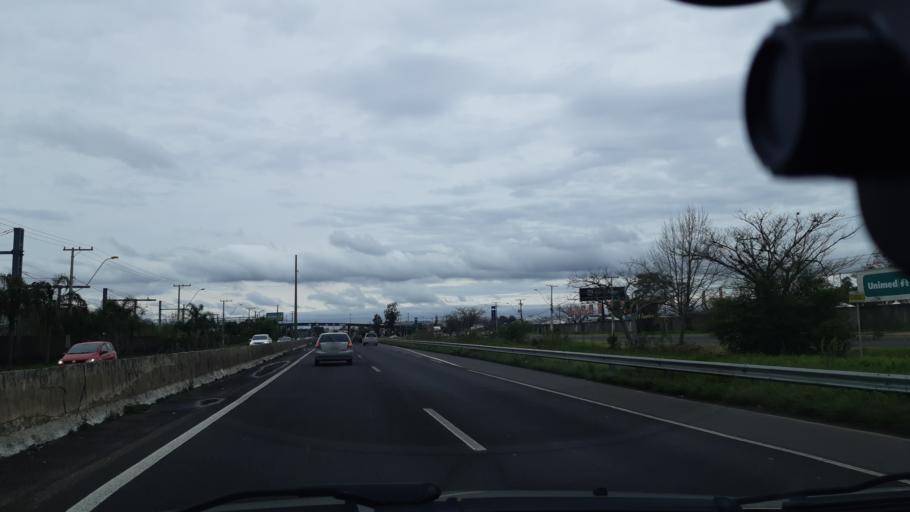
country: BR
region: Rio Grande do Sul
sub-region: Esteio
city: Esteio
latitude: -29.8556
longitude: -51.1803
